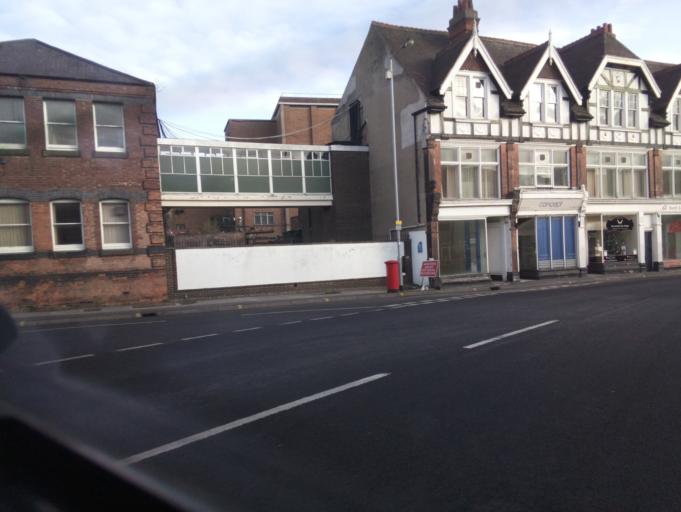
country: GB
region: England
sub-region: Staffordshire
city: Burton upon Trent
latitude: 52.8060
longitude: -1.6399
